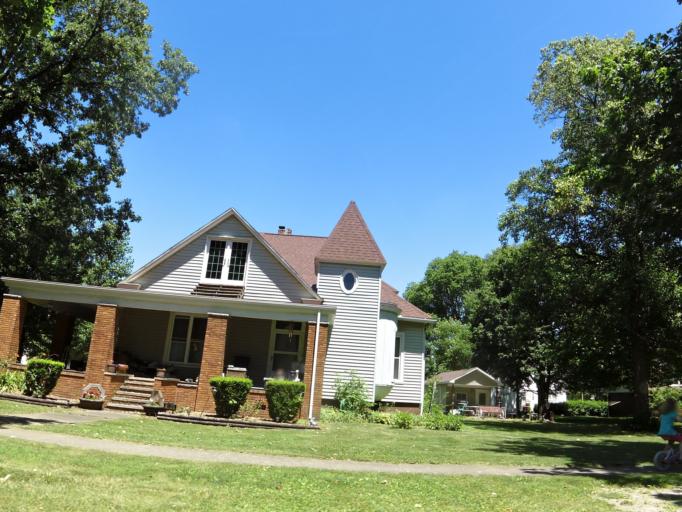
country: US
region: Illinois
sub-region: Iroquois County
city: Milford
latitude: 40.6284
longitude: -87.6916
